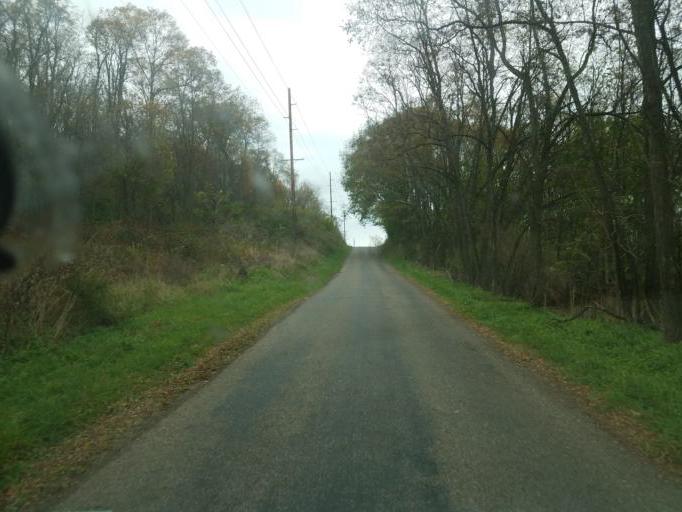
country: US
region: Ohio
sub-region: Ashland County
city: Loudonville
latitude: 40.6616
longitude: -82.2117
